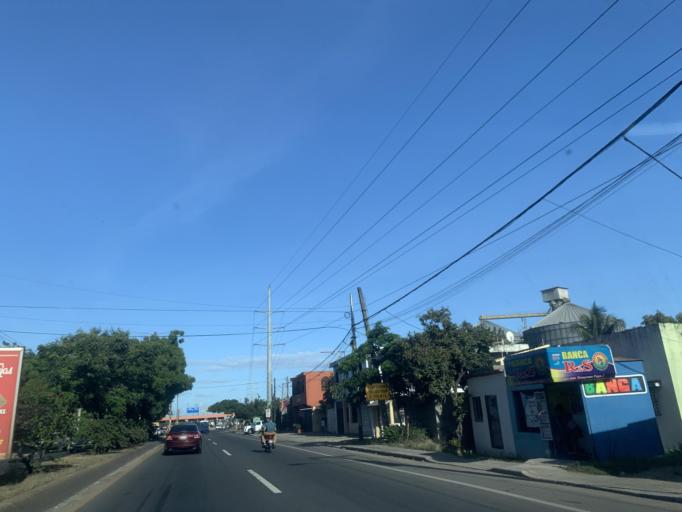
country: DO
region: San Cristobal
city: El Carril
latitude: 18.4303
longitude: -70.0037
